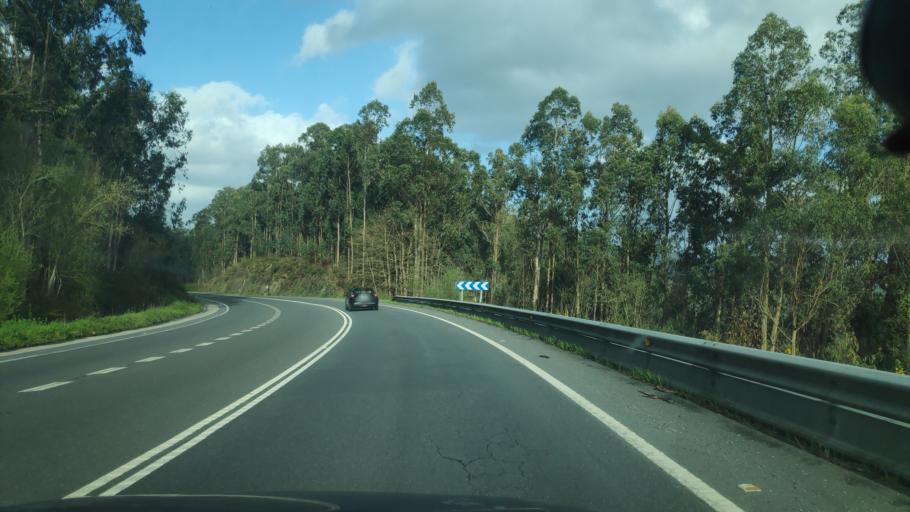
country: ES
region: Galicia
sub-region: Provincia da Coruna
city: Ames
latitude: 42.8761
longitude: -8.6706
